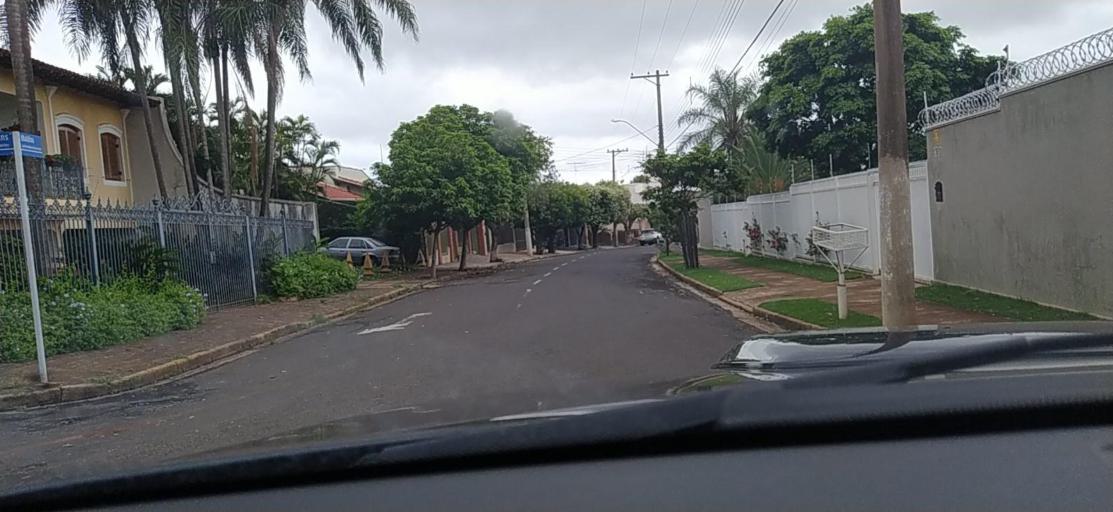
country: BR
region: Sao Paulo
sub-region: Olimpia
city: Olimpia
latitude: -20.7338
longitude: -48.9156
